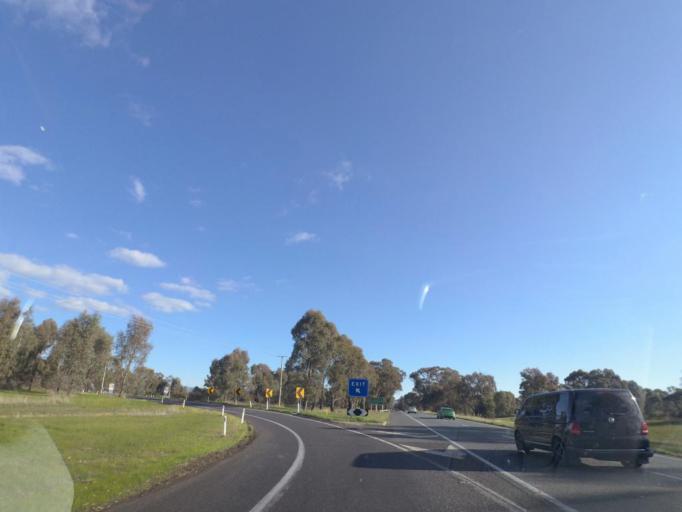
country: AU
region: Victoria
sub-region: Benalla
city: Benalla
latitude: -36.6940
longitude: 145.6594
